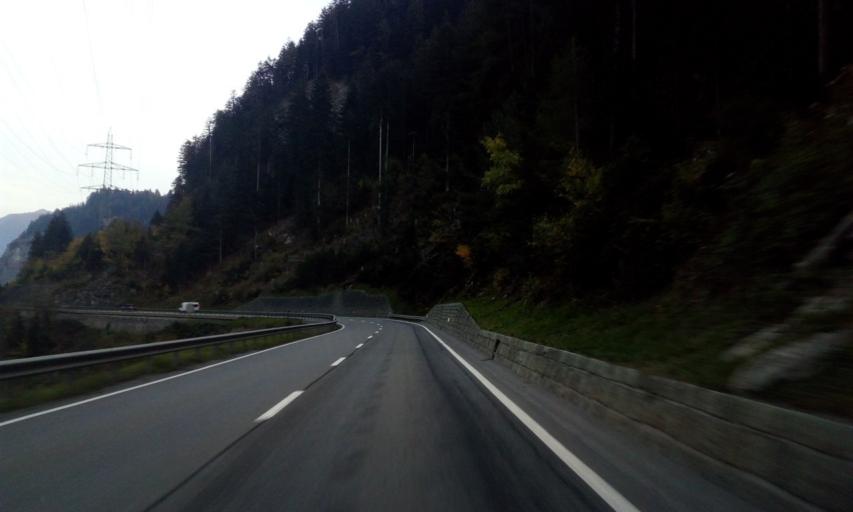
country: CH
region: Grisons
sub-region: Hinterrhein District
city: Thusis
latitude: 46.6921
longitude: 9.4938
